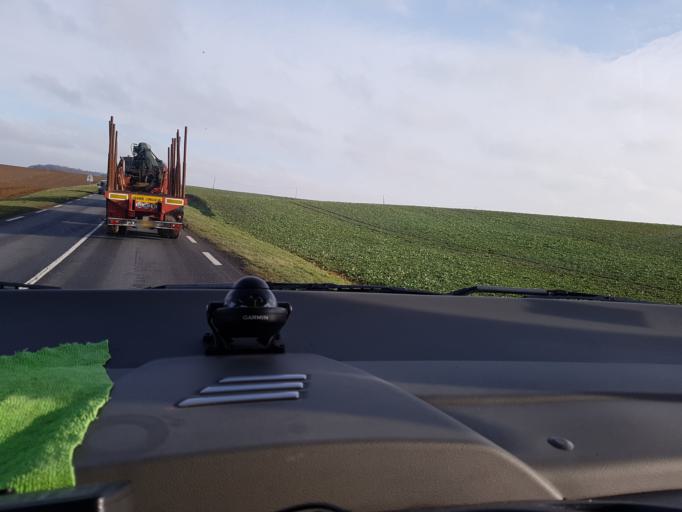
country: FR
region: Picardie
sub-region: Departement de l'Aisne
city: Saint-Michel
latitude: 49.8757
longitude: 4.1453
